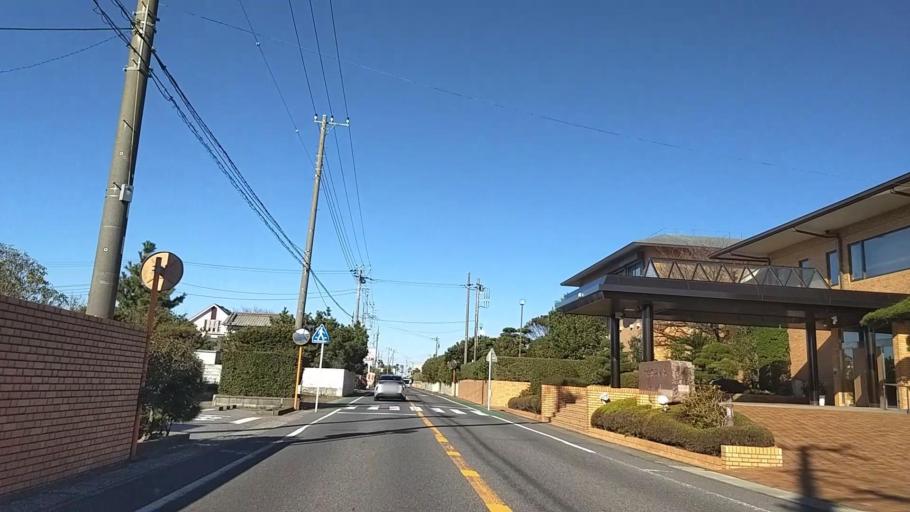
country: JP
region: Chiba
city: Mobara
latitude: 35.3750
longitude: 140.3876
